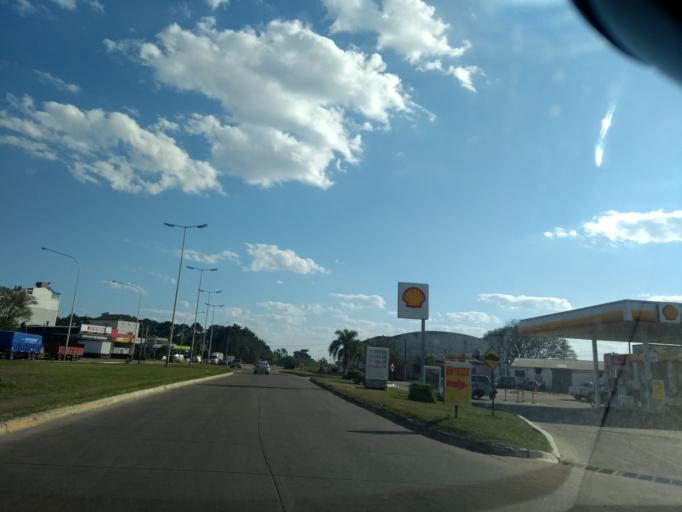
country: AR
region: Corrientes
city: Corrientes
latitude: -27.4833
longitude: -58.7825
